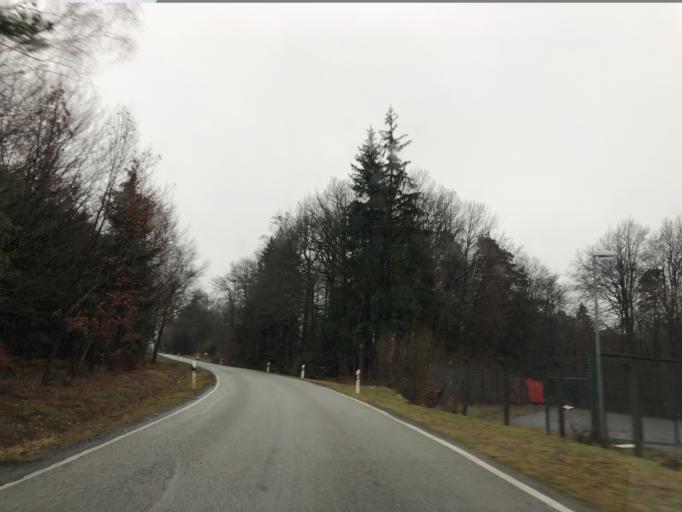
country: DE
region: Hesse
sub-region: Regierungsbezirk Darmstadt
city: Lutzelbach
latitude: 49.7451
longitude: 9.0806
